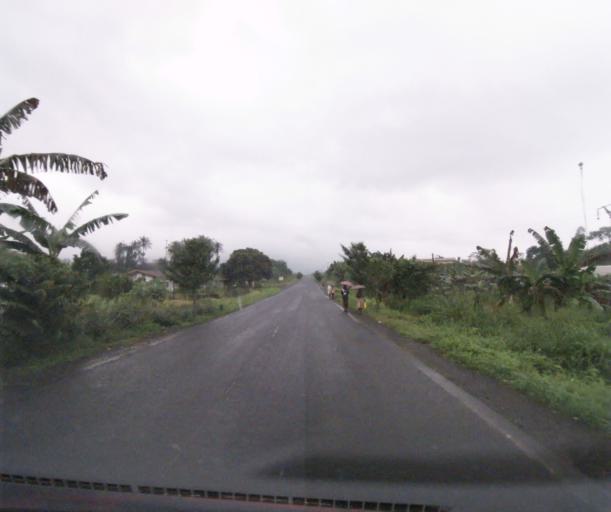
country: CM
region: South-West Province
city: Idenao
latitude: 4.2089
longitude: 8.9928
